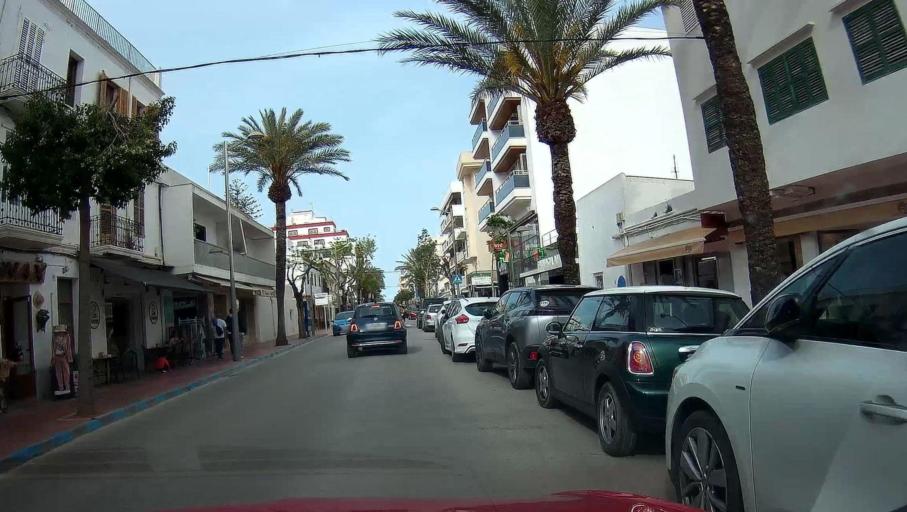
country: ES
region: Balearic Islands
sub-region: Illes Balears
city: Santa Eularia des Riu
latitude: 38.9850
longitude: 1.5341
